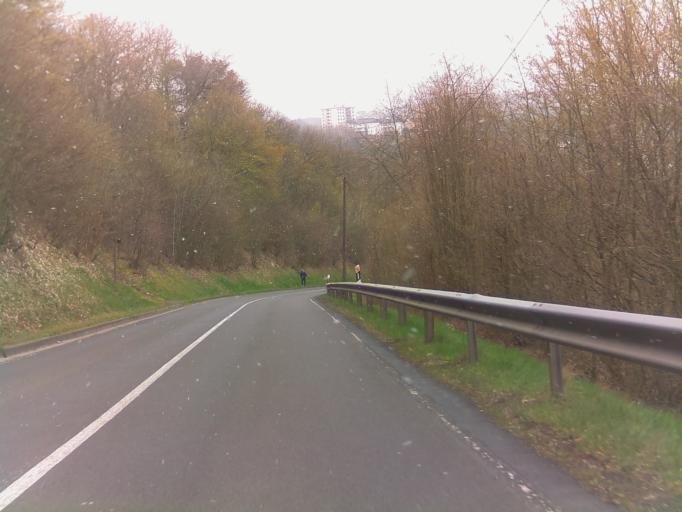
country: DE
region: Rheinland-Pfalz
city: Vollmersbach
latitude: 49.7230
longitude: 7.3238
